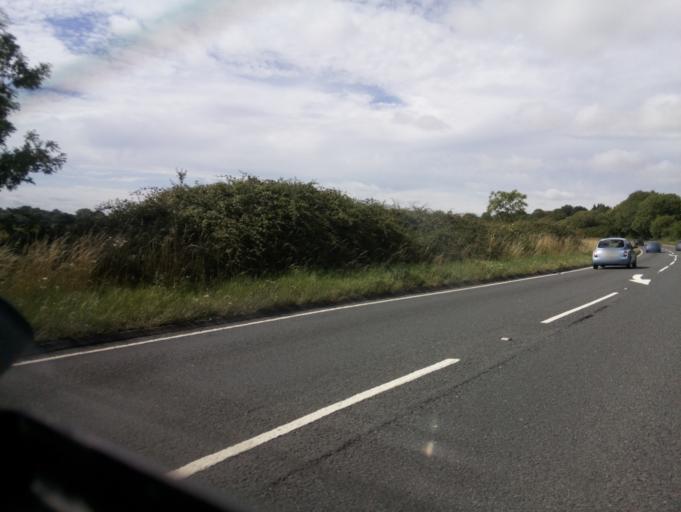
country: GB
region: England
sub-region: Dorset
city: Dorchester
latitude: 50.7302
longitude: -2.4610
